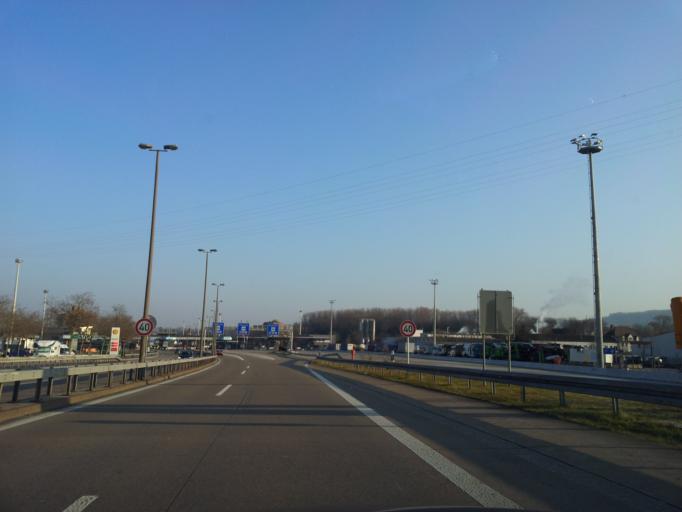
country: DE
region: Baden-Wuerttemberg
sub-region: Freiburg Region
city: Weil am Rhein
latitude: 47.5934
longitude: 7.6040
